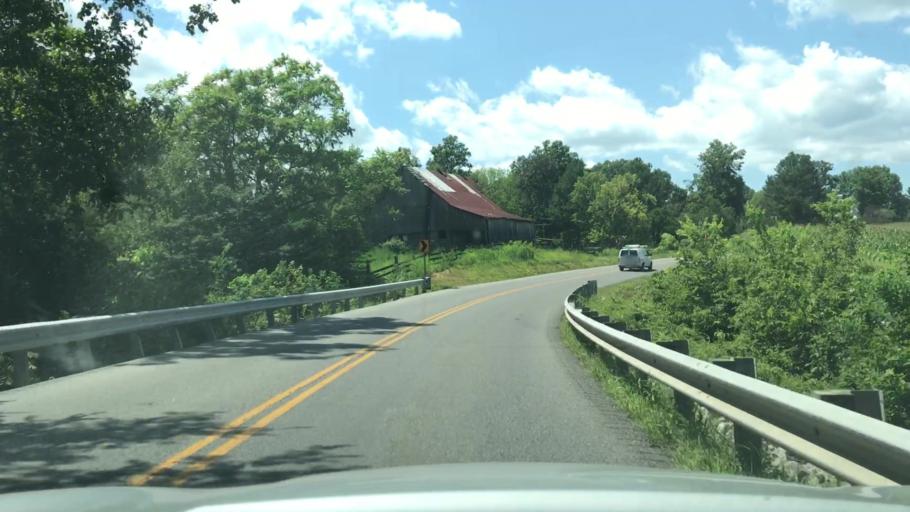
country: US
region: Kentucky
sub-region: Christian County
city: Hopkinsville
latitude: 36.8892
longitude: -87.4585
